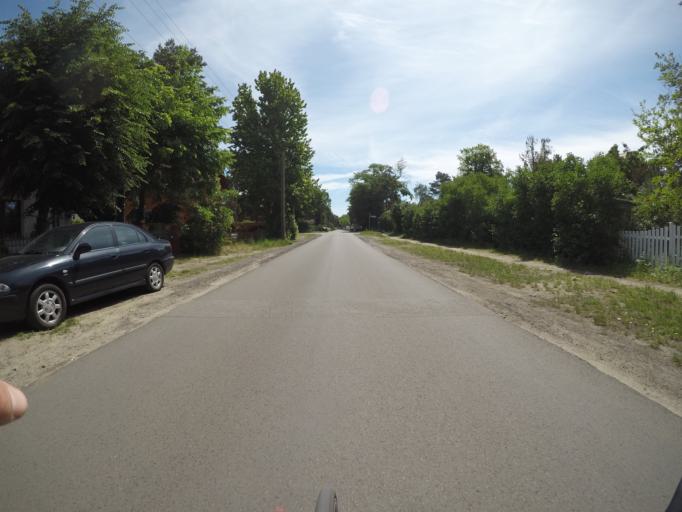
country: DE
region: Berlin
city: Mahlsdorf
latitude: 52.4934
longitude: 13.6153
